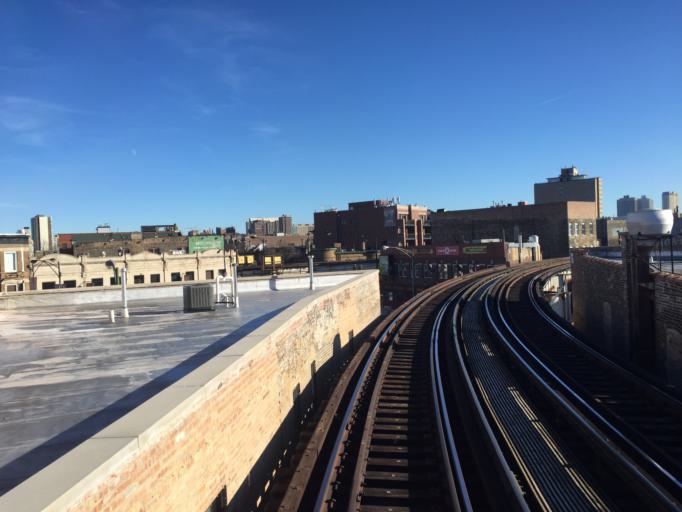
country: US
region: Illinois
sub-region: Cook County
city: Chicago
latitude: 41.9438
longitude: -87.6545
